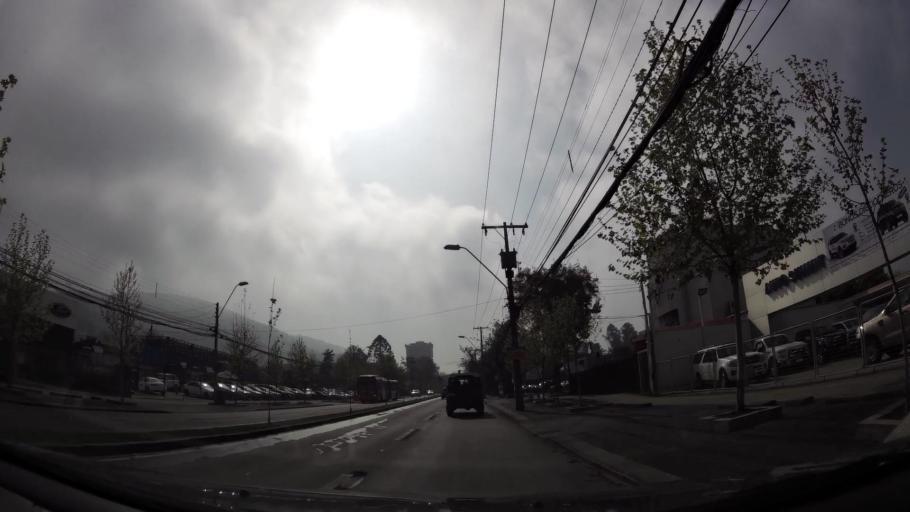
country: CL
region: Santiago Metropolitan
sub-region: Provincia de Santiago
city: Villa Presidente Frei, Nunoa, Santiago, Chile
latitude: -33.3811
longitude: -70.5441
